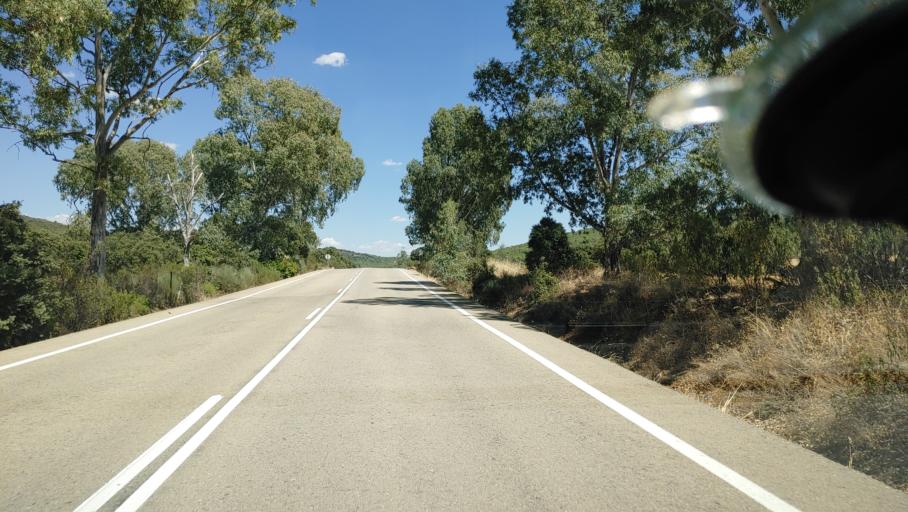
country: ES
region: Castille-La Mancha
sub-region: Provincia de Ciudad Real
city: Saceruela
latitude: 38.9844
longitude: -4.5566
